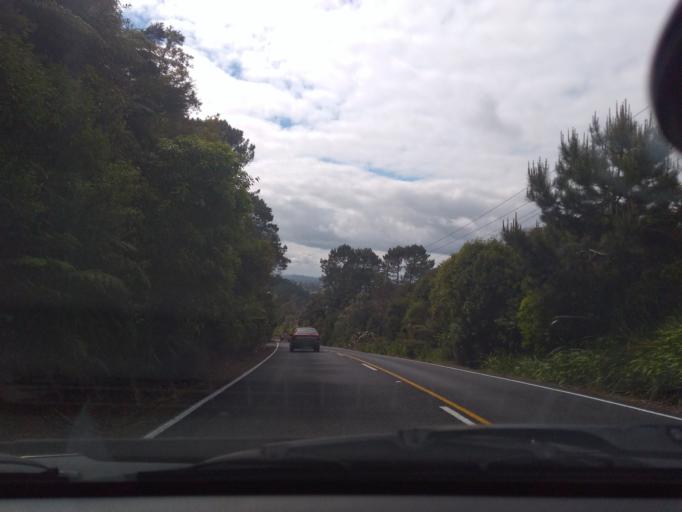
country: NZ
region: Auckland
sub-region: Auckland
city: Rosebank
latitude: -36.8613
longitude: 174.5560
